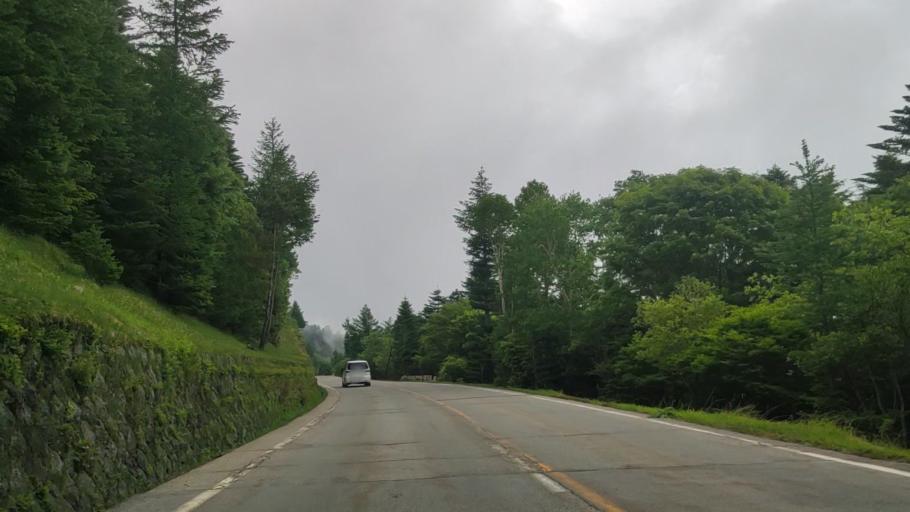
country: JP
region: Yamanashi
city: Fujikawaguchiko
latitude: 35.3871
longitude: 138.6905
